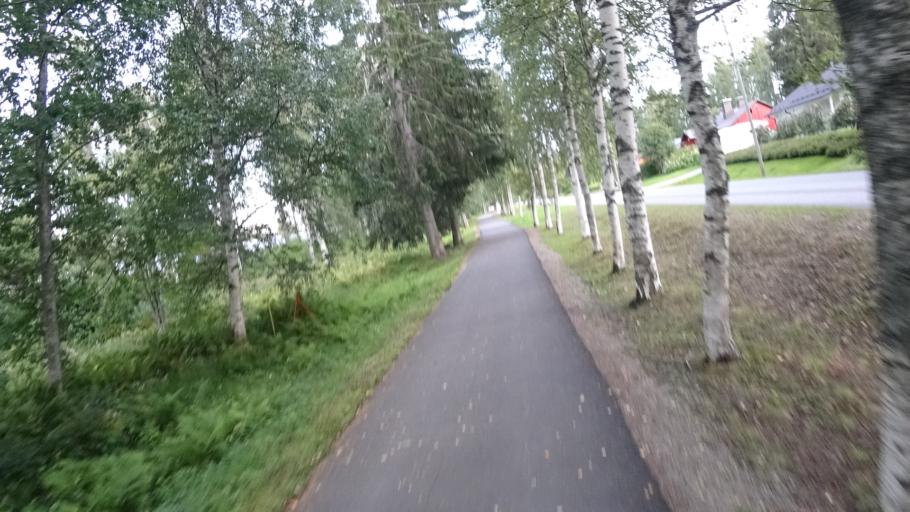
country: FI
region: North Karelia
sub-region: Joensuu
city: Ilomantsi
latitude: 62.6752
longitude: 30.9195
